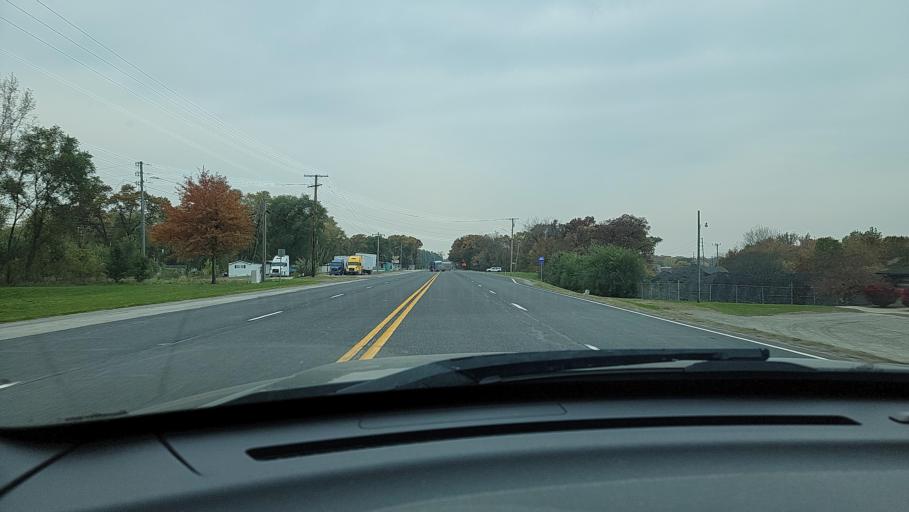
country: US
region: Indiana
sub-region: Porter County
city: Portage
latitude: 41.5945
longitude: -87.1896
